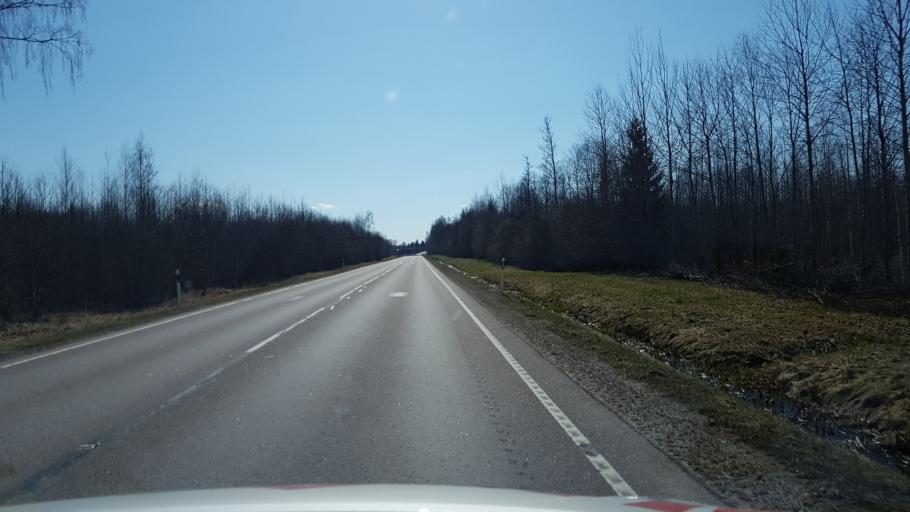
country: EE
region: Jogevamaa
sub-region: Mustvee linn
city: Mustvee
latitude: 58.7610
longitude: 26.8856
